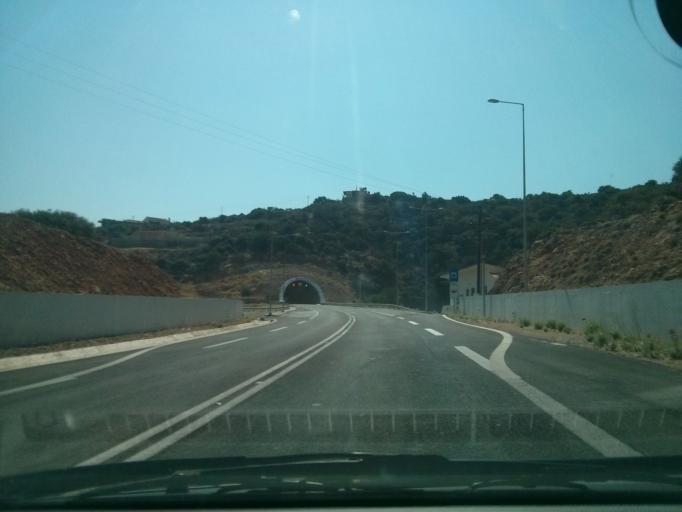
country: GR
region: Crete
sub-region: Nomos Lasithiou
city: Agios Nikolaos
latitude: 35.1622
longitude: 25.7061
